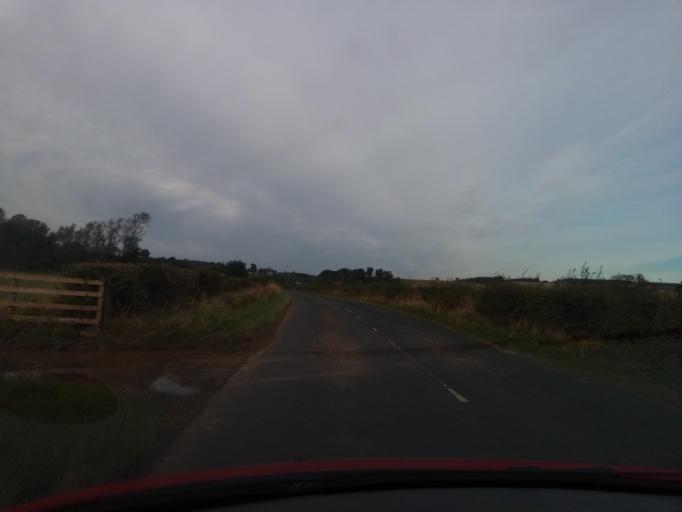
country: GB
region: Scotland
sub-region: The Scottish Borders
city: Kelso
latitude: 55.5219
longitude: -2.3989
